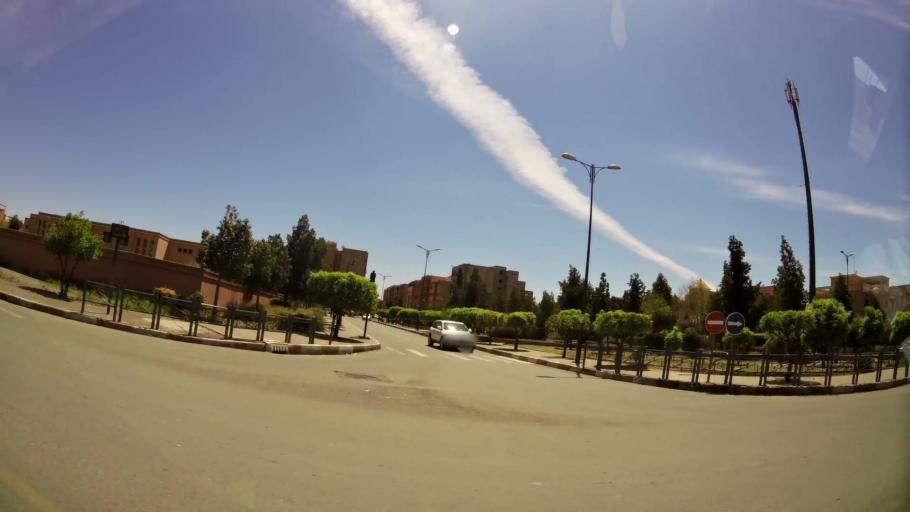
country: MA
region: Marrakech-Tensift-Al Haouz
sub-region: Marrakech
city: Marrakesh
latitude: 31.6384
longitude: -8.0580
